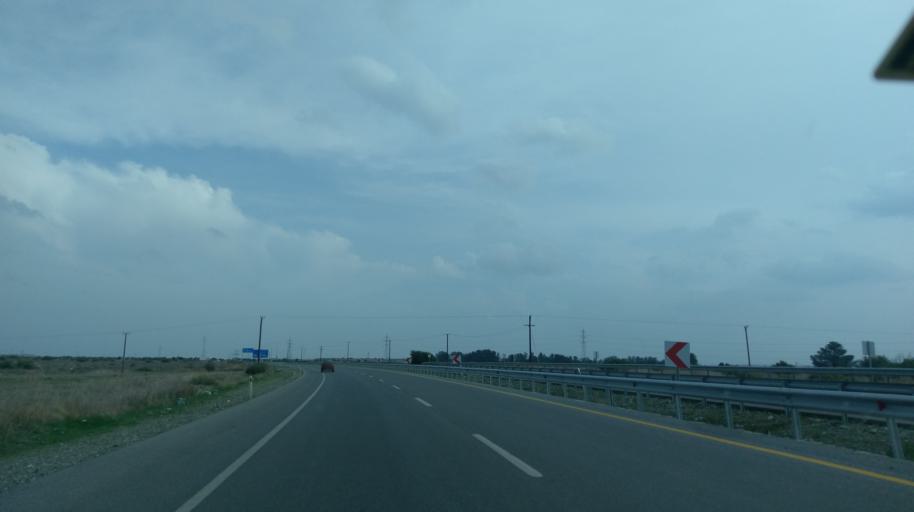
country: CY
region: Lefkosia
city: Astromeritis
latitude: 35.1960
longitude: 33.0562
